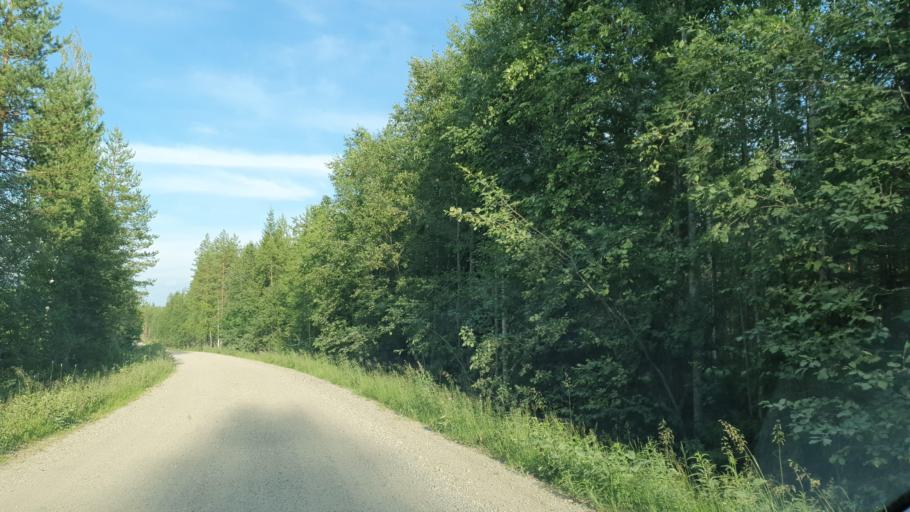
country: FI
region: Kainuu
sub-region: Kehys-Kainuu
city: Kuhmo
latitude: 64.2851
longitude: 29.7561
